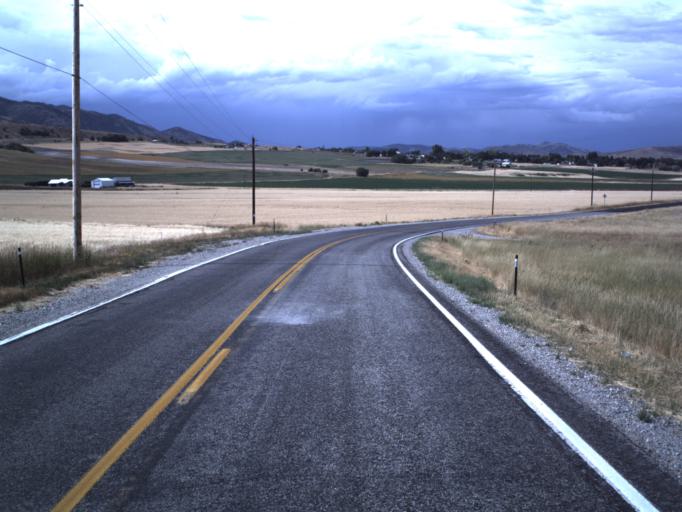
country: US
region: Utah
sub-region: Cache County
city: Benson
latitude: 41.8981
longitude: -112.0453
